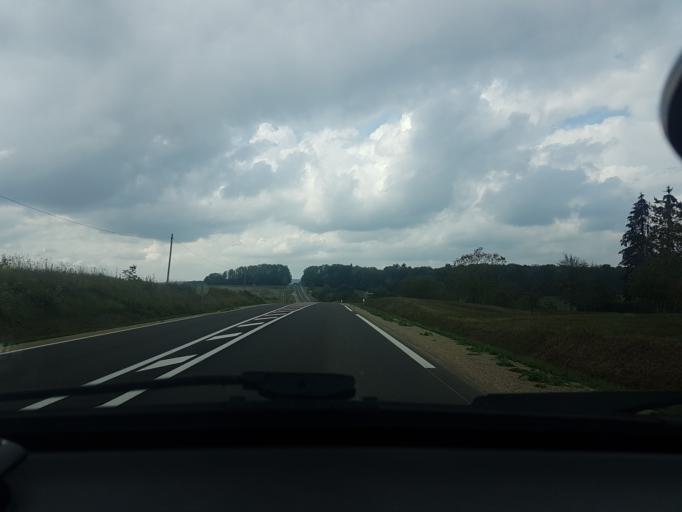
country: FR
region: Franche-Comte
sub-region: Departement de la Haute-Saone
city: Villersexel
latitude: 47.5460
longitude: 6.4595
